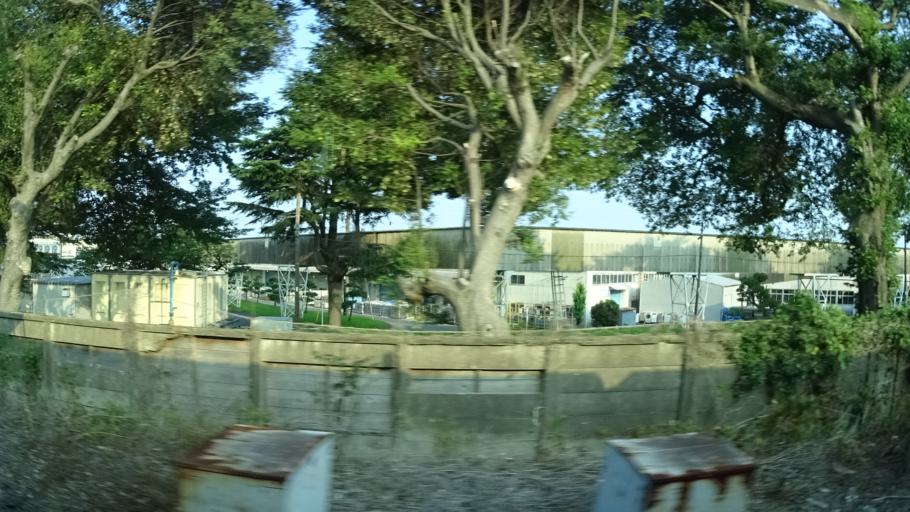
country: JP
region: Ibaraki
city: Hitachi
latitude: 36.5543
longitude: 140.6355
